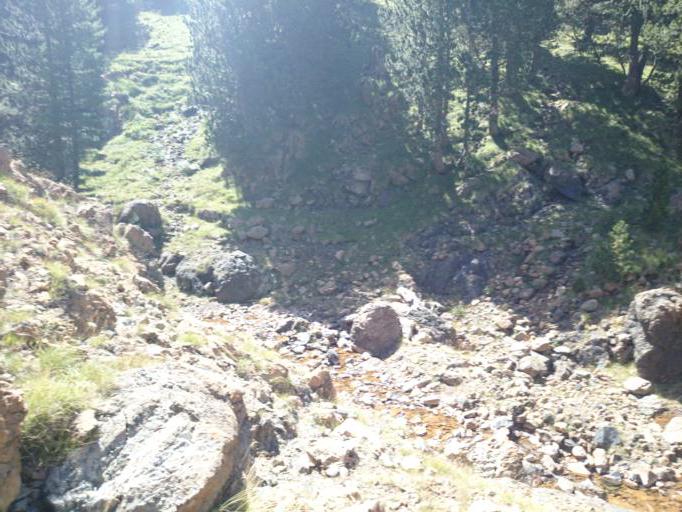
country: AL
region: Korce
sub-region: Rrethi i Korces
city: Moglice
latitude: 40.7621
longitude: 20.4418
